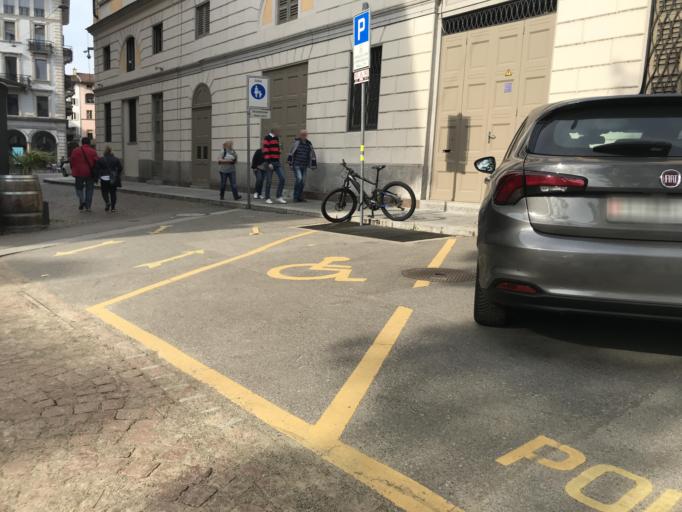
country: CH
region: Ticino
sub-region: Lugano District
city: Lugano
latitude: 46.0033
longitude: 8.9511
